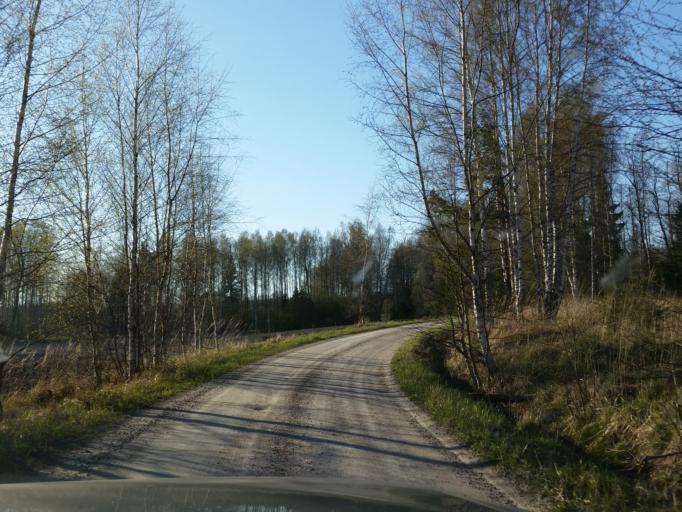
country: FI
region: Uusimaa
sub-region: Helsinki
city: Espoo
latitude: 60.1128
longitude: 24.6245
